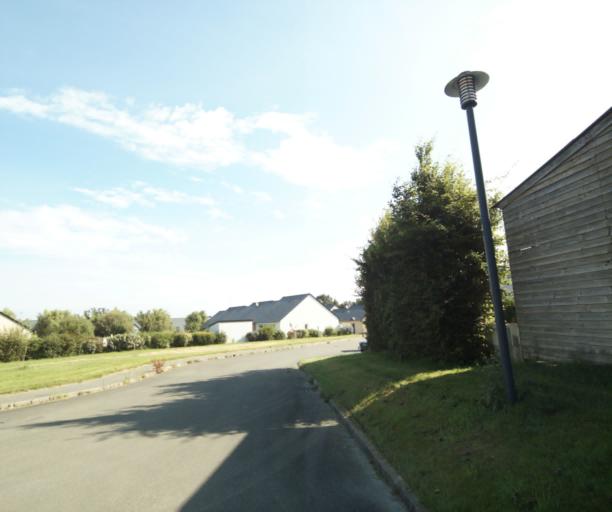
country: FR
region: Pays de la Loire
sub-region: Departement de la Mayenne
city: Laval
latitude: 48.0538
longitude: -0.7797
